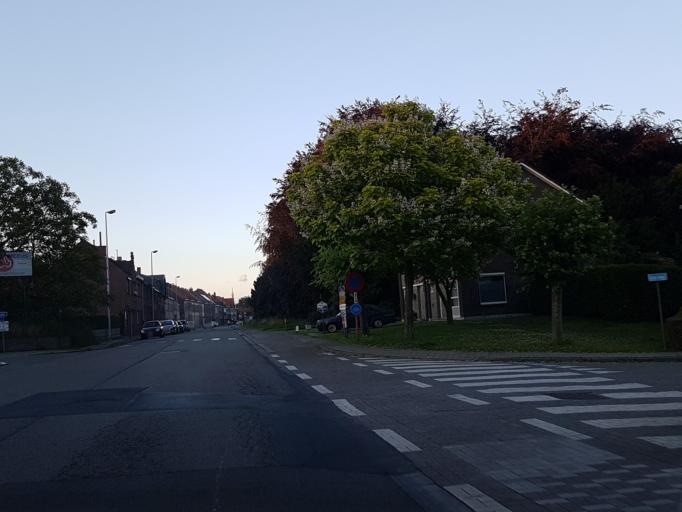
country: BE
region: Flanders
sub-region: Provincie Oost-Vlaanderen
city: Temse
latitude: 51.1222
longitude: 4.1978
